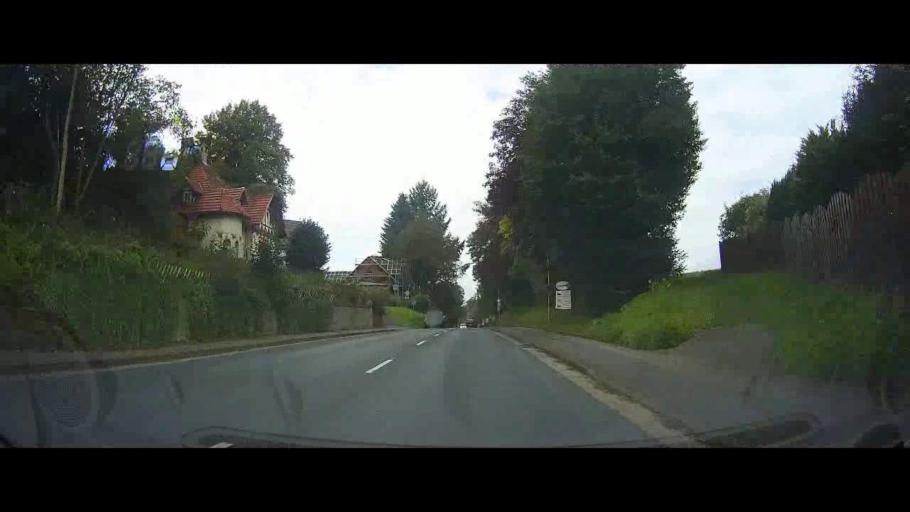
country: DE
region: Lower Saxony
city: Uslar
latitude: 51.6550
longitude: 9.6474
